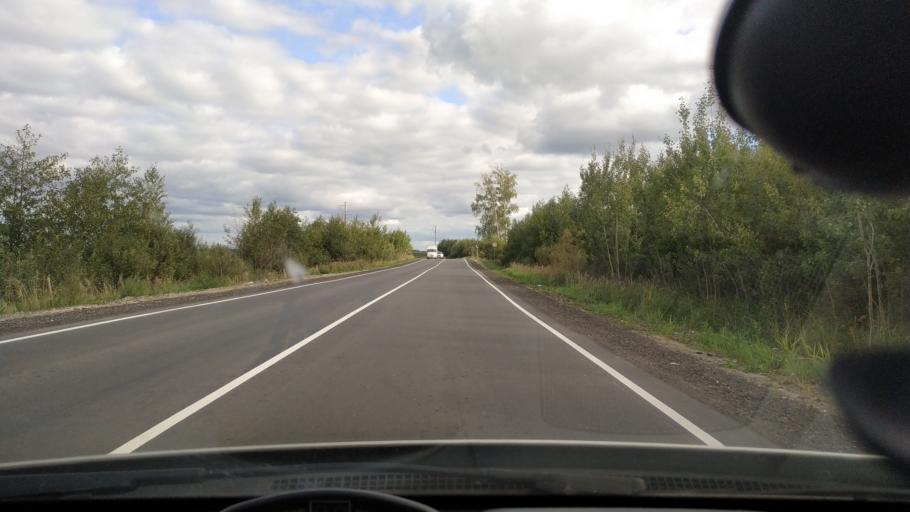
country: RU
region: Moskovskaya
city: Vereya
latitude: 55.7250
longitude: 39.0472
